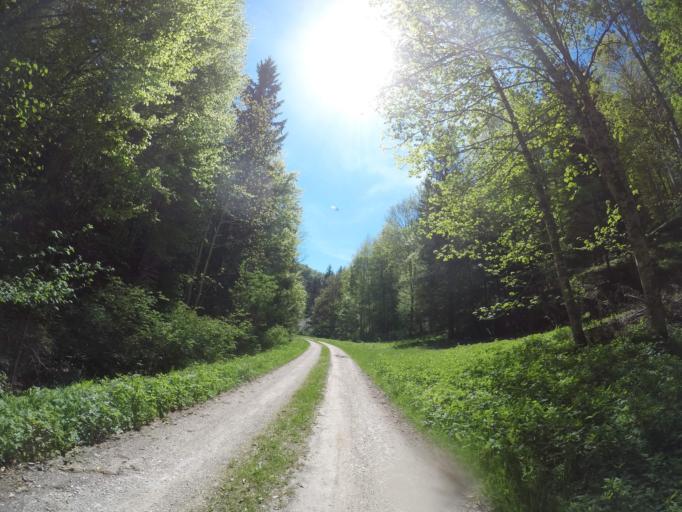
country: DE
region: Baden-Wuerttemberg
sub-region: Tuebingen Region
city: Schelklingen
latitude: 48.4121
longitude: 9.7193
